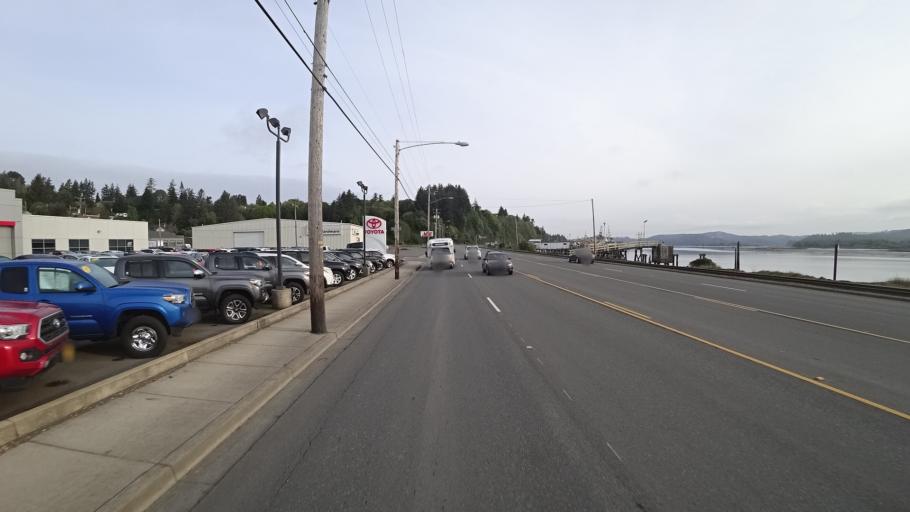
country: US
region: Oregon
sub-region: Coos County
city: Coos Bay
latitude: 43.3824
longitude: -124.2202
